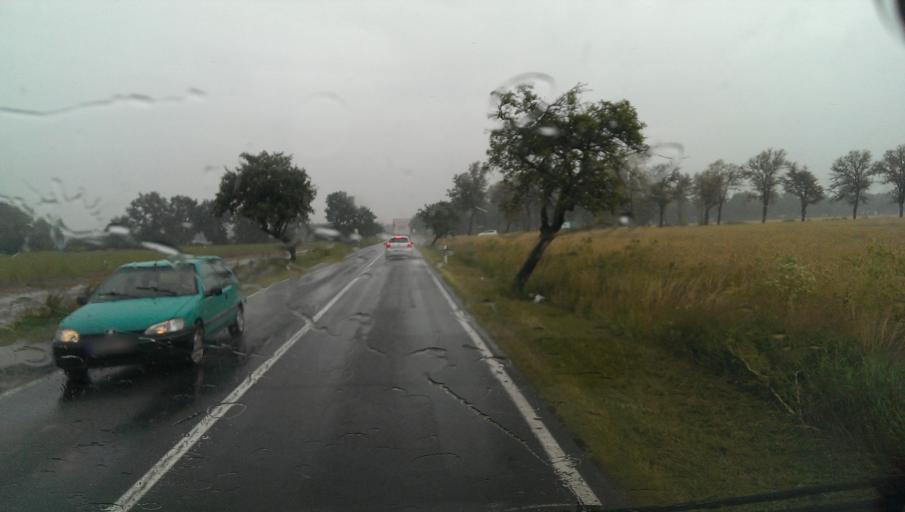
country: DE
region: Brandenburg
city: Roskow
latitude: 52.4784
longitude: 12.6971
